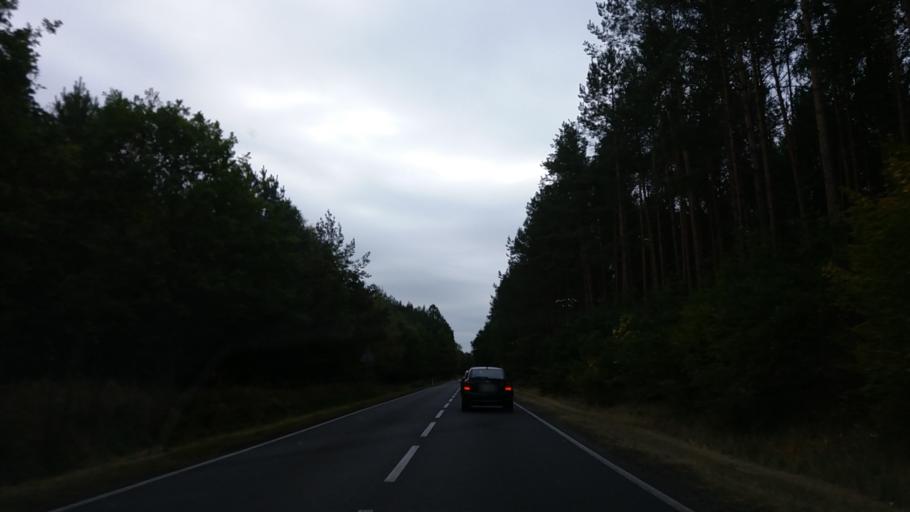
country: PL
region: Lubusz
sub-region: Powiat gorzowski
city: Klodawa
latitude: 52.8308
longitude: 15.2080
